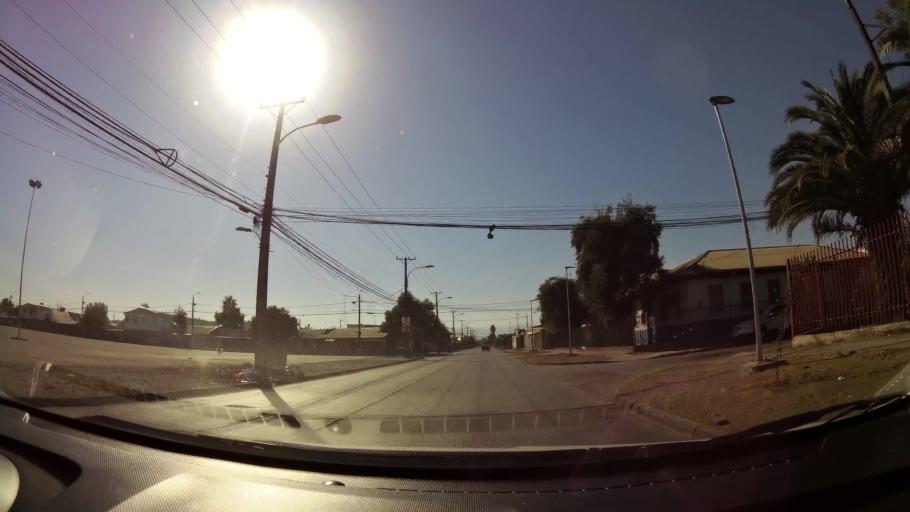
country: CL
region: Maule
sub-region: Provincia de Curico
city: Curico
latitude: -34.9969
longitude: -71.2554
